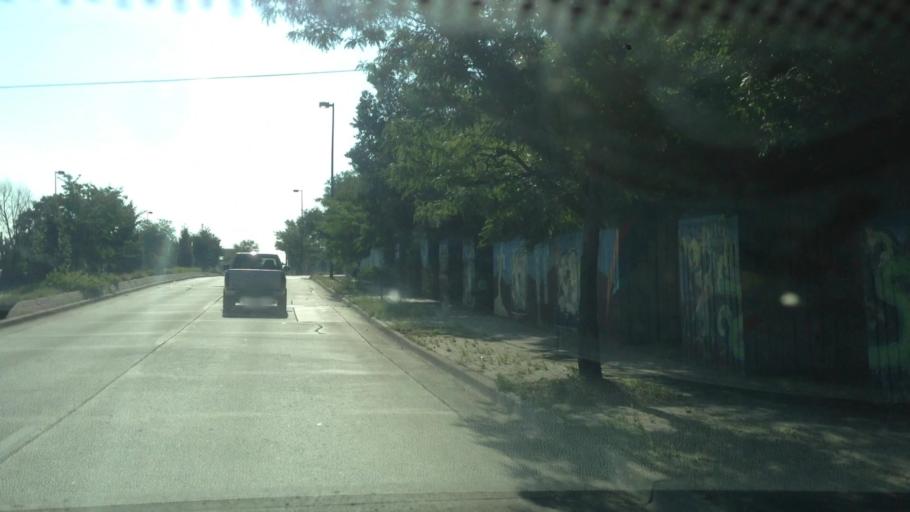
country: US
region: Colorado
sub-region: Jefferson County
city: Lakewood
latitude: 39.7112
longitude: -105.0372
